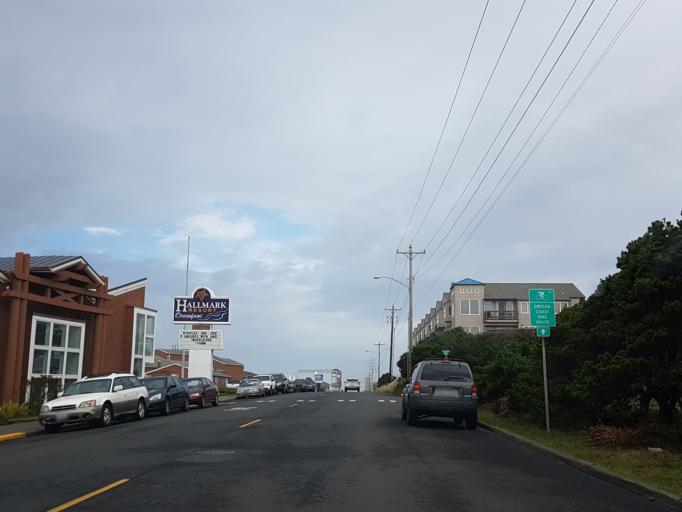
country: US
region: Oregon
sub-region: Lincoln County
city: Newport
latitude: 44.6297
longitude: -124.0634
